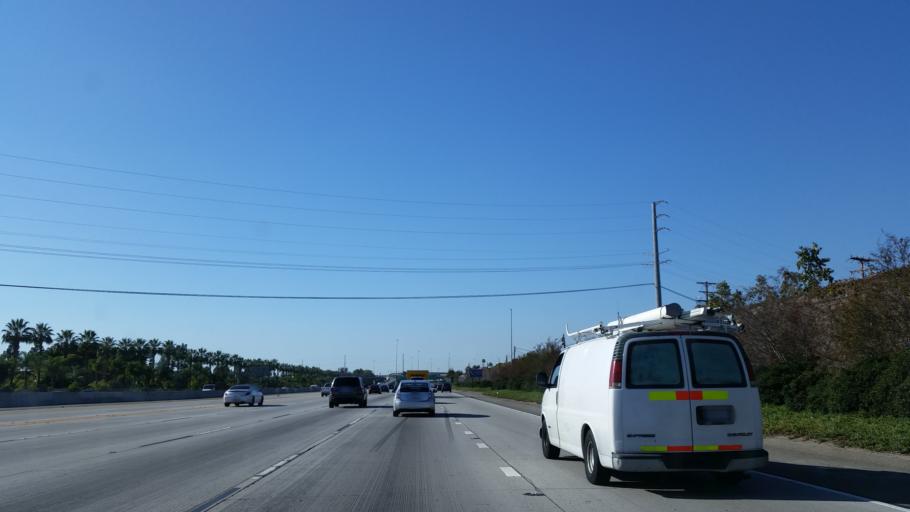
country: US
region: California
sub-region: Orange County
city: Buena Park
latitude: 33.8497
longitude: -117.9670
